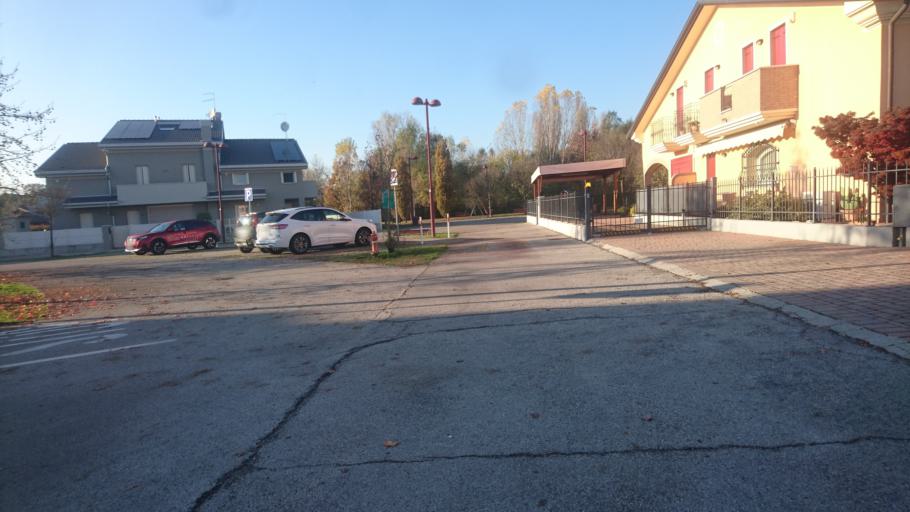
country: IT
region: Veneto
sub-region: Provincia di Padova
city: Villaguattera
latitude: 45.4473
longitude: 11.8157
